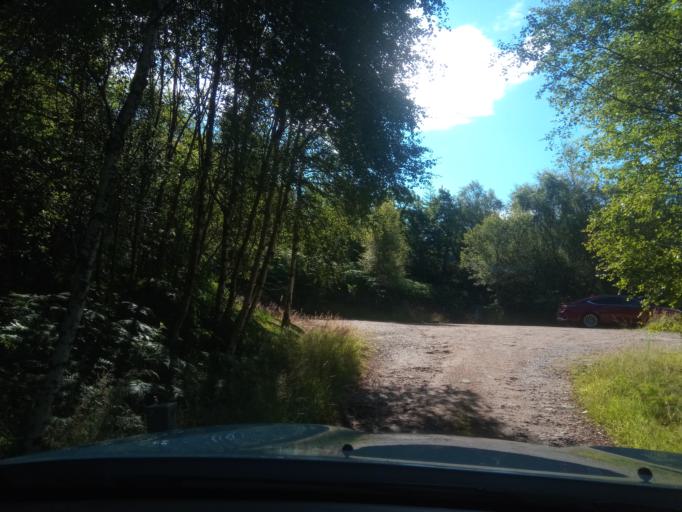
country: GB
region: Scotland
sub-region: Argyll and Bute
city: Isle Of Mull
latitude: 56.6982
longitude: -5.6896
